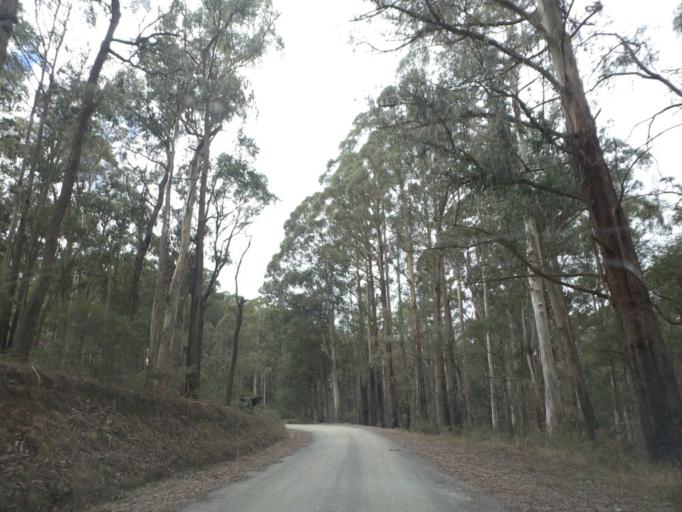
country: AU
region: Victoria
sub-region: Murrindindi
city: Alexandra
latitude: -37.4591
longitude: 145.9715
